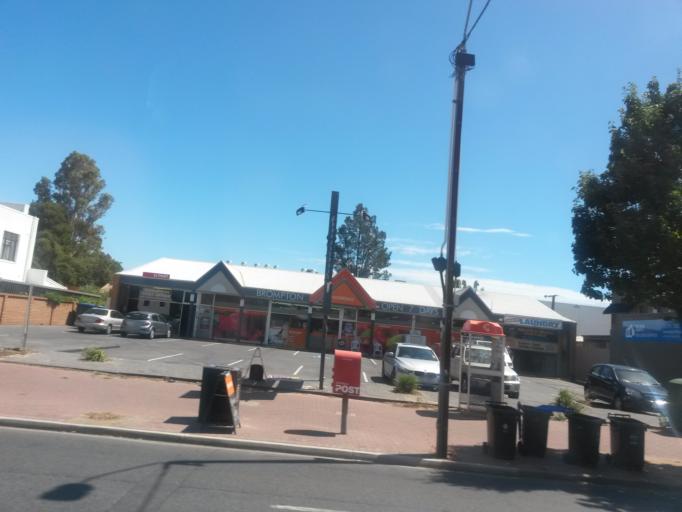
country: AU
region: South Australia
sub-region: Adelaide
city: North Adelaide
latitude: -34.8942
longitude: 138.5797
